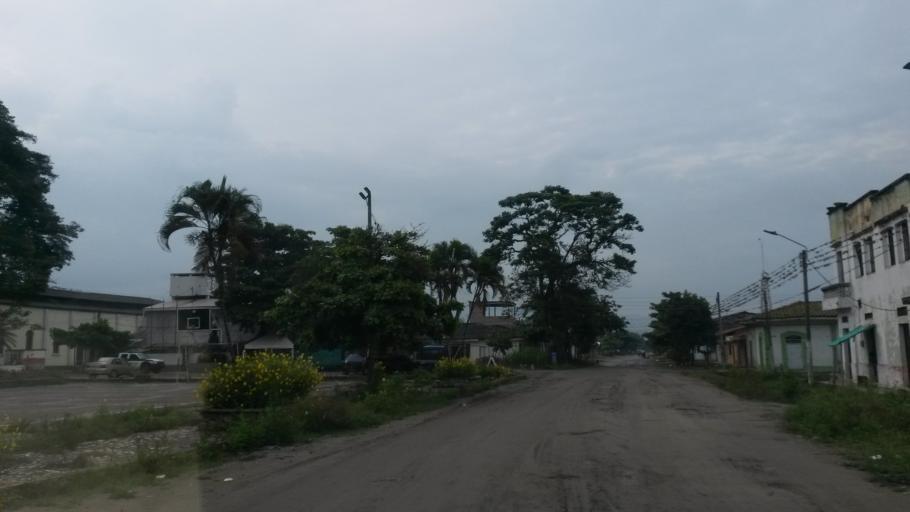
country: CO
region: Cauca
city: Padilla
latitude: 3.2253
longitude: -76.3145
